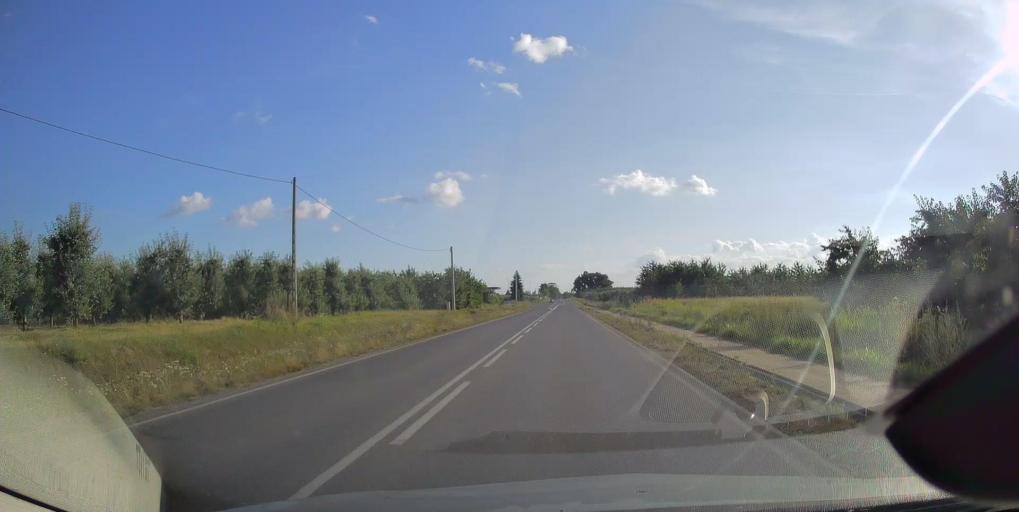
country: PL
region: Masovian Voivodeship
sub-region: Powiat grojecki
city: Belsk Duzy
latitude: 51.8390
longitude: 20.8266
